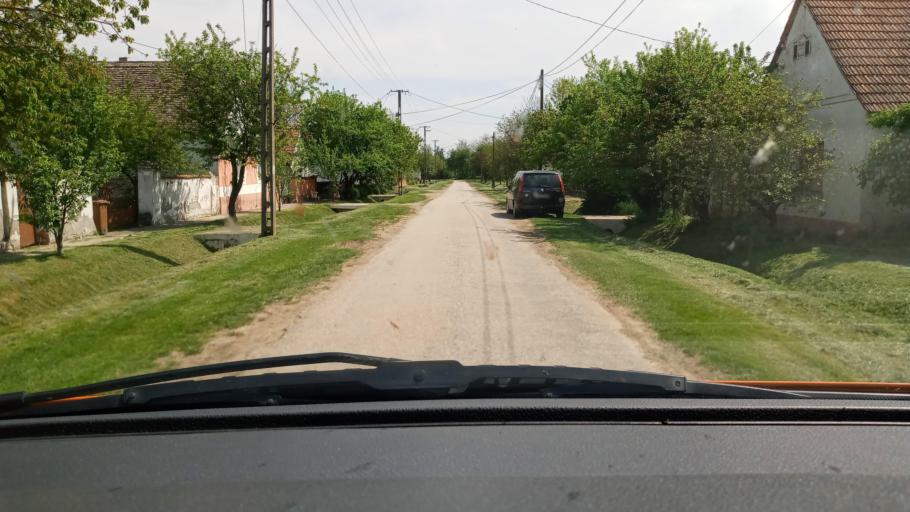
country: HR
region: Osjecko-Baranjska
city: Beli Manastir
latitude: 45.7975
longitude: 18.5256
